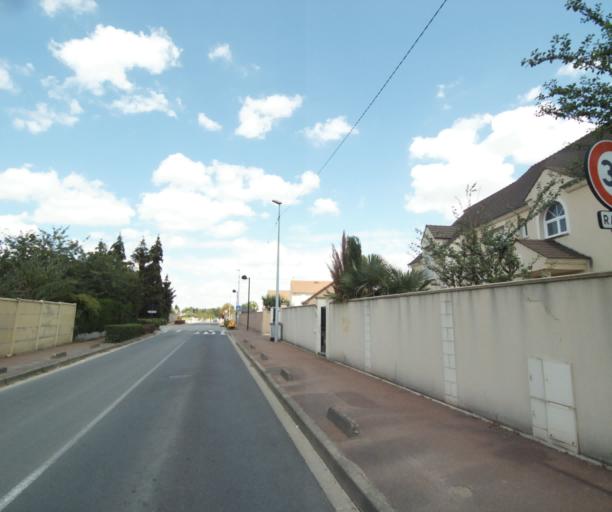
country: FR
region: Ile-de-France
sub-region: Departement de Seine-et-Marne
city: Samoreau
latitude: 48.4375
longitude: 2.7553
